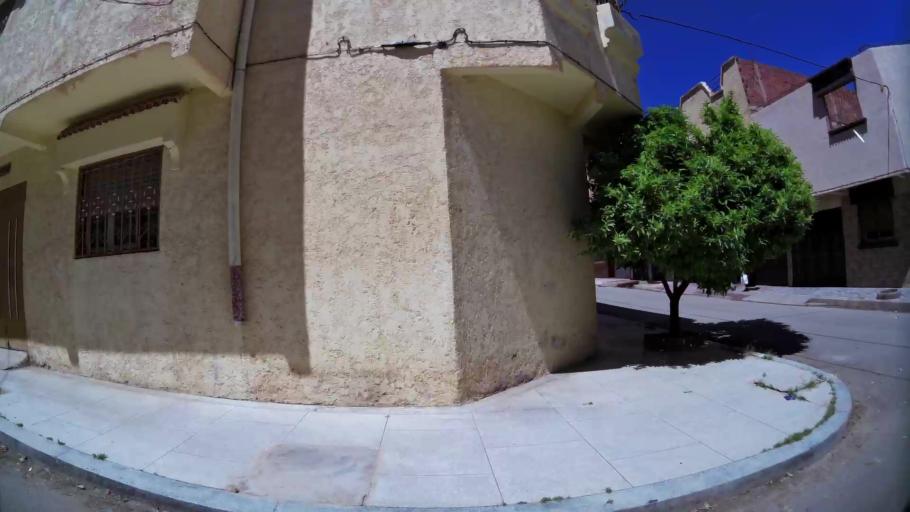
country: MA
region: Oriental
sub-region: Oujda-Angad
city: Oujda
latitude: 34.6583
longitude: -1.9404
